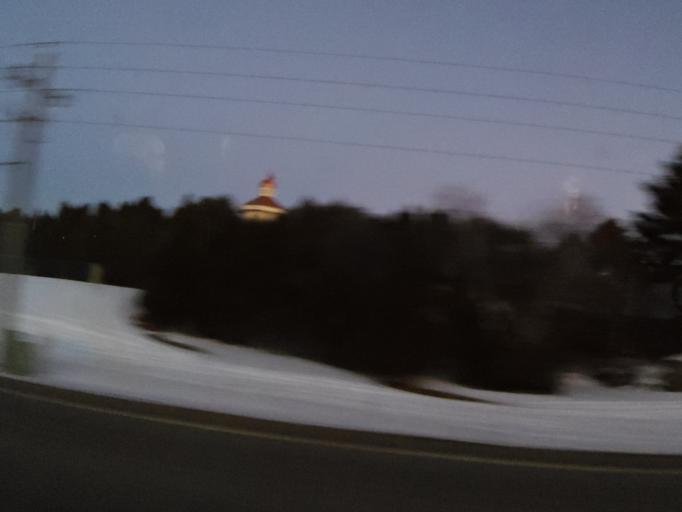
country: US
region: Minnesota
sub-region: Scott County
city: Shakopee
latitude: 44.7506
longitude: -93.5204
